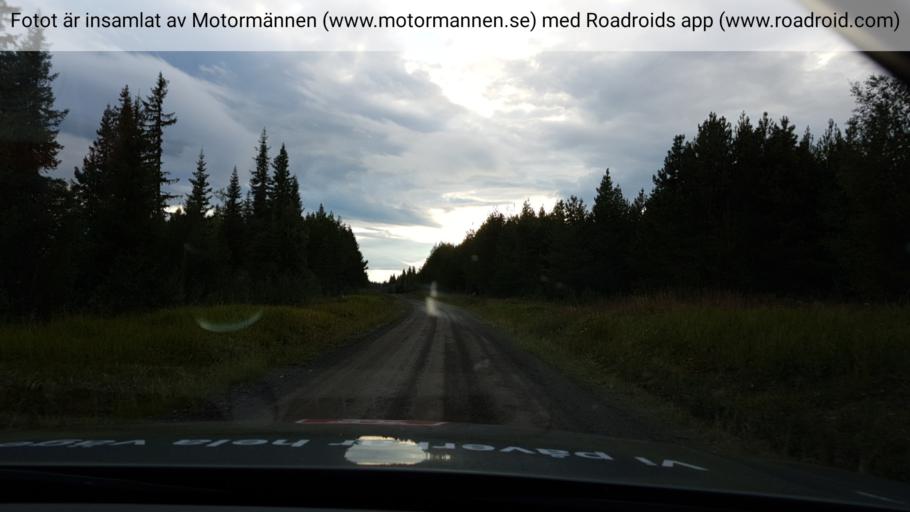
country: SE
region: Jaemtland
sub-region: OEstersunds Kommun
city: Lit
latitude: 63.4973
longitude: 15.1671
